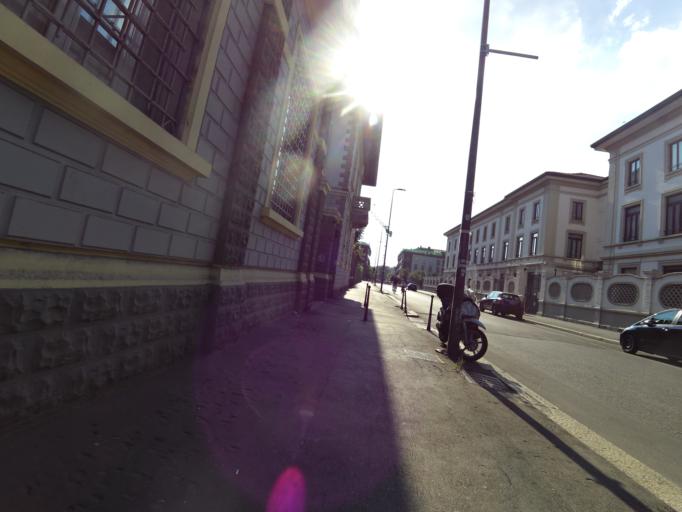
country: IT
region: Lombardy
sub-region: Citta metropolitana di Milano
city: Milano
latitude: 45.4454
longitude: 9.1740
